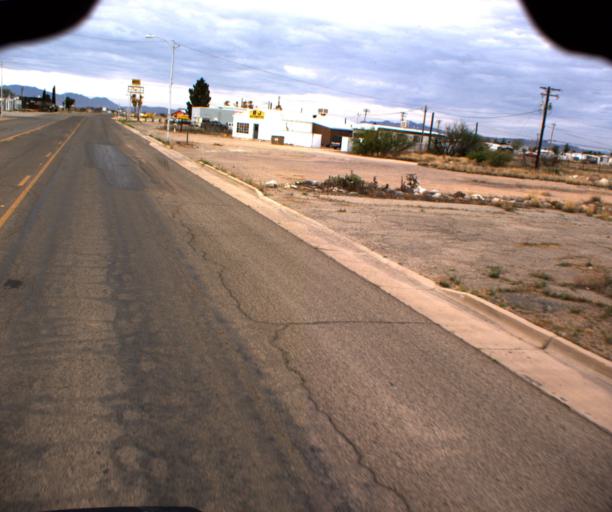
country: US
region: Arizona
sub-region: Cochise County
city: Willcox
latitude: 32.2465
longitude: -109.8364
